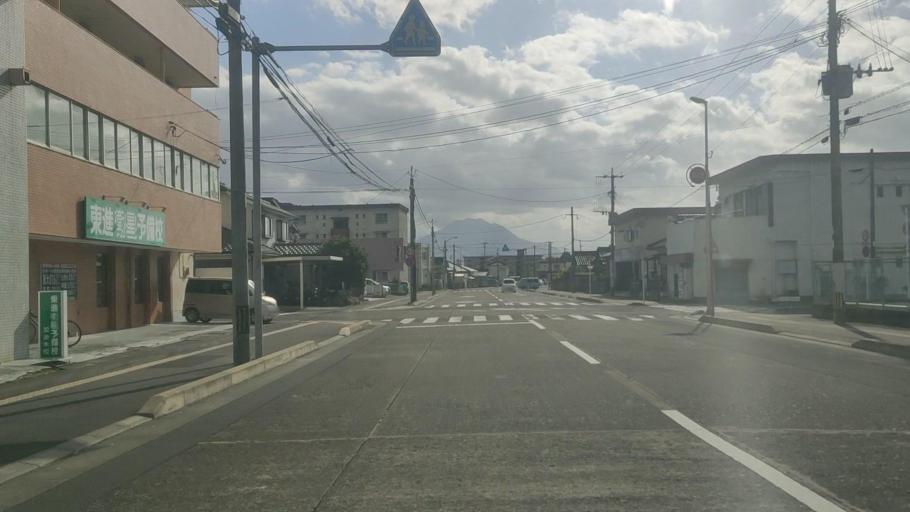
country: JP
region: Kagoshima
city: Kajiki
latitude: 31.7368
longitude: 130.6702
